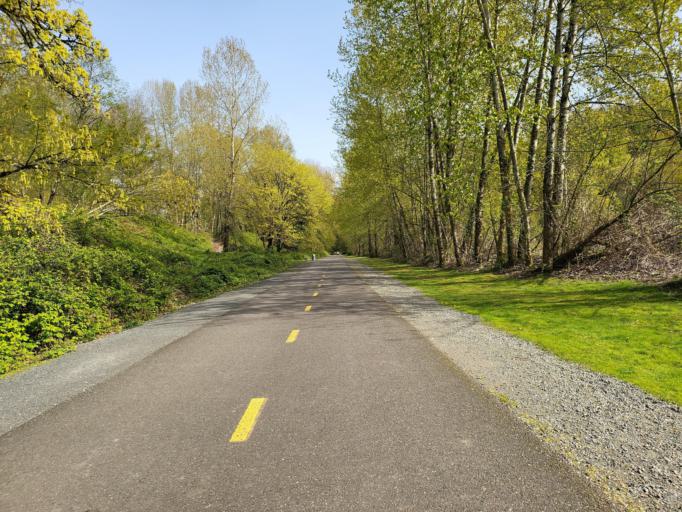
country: US
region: Washington
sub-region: King County
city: Renton
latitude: 47.4784
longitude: -122.1943
